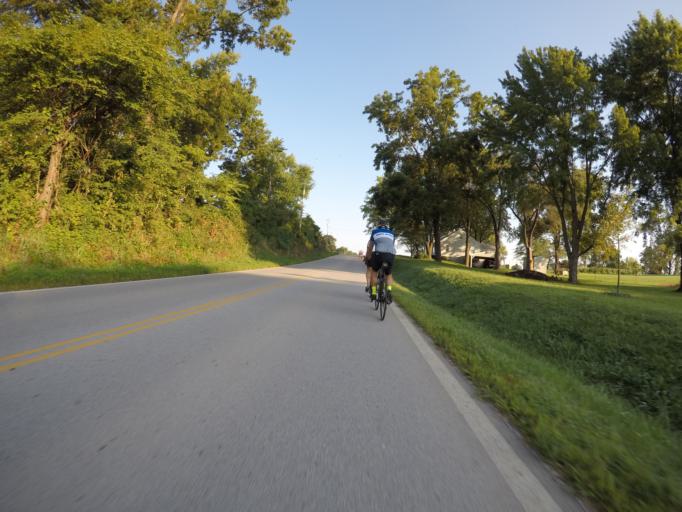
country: US
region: Kansas
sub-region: Leavenworth County
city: Lansing
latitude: 39.2467
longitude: -94.8740
